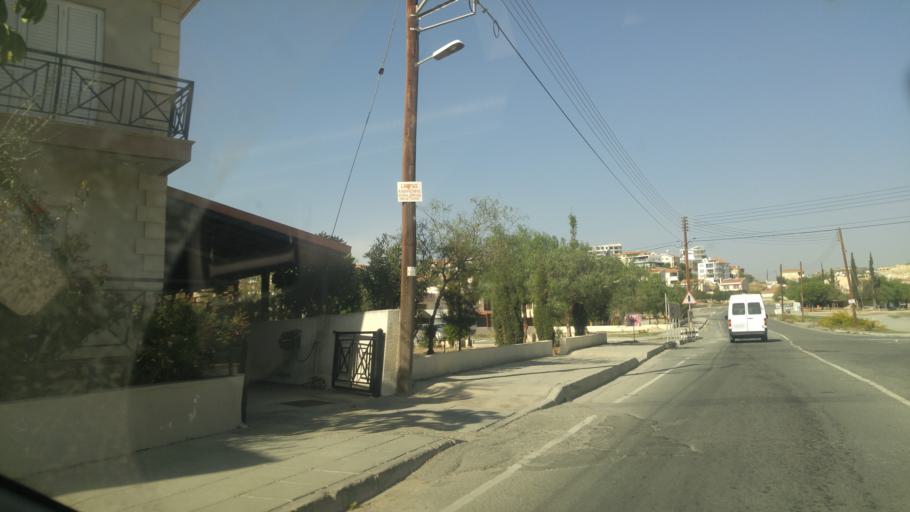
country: CY
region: Limassol
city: Limassol
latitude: 34.7090
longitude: 33.0383
